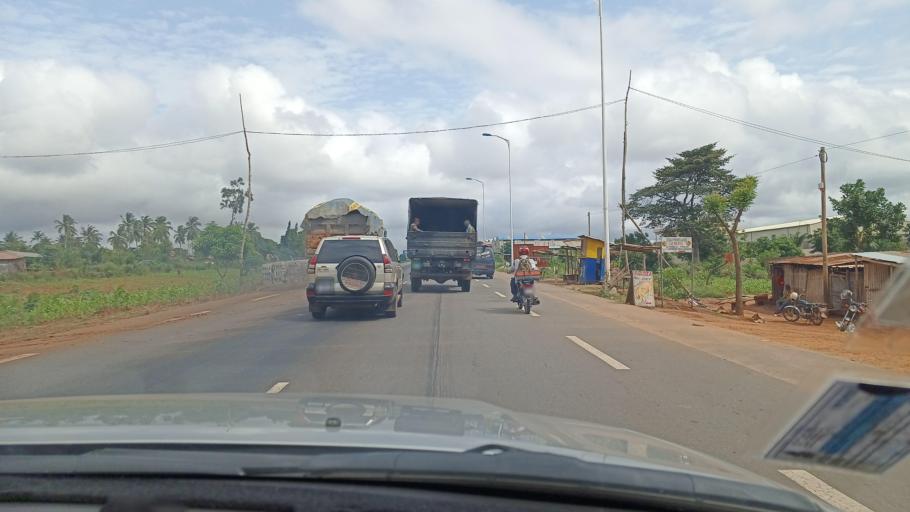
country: TG
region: Maritime
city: Tsevie
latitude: 6.3616
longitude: 1.2094
